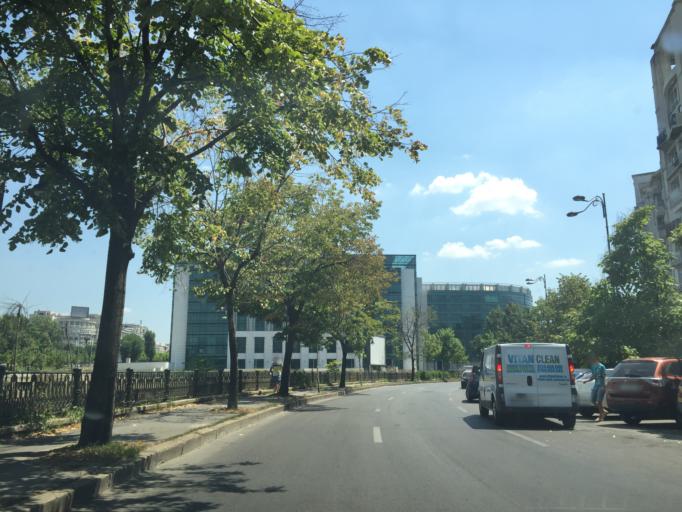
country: RO
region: Bucuresti
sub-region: Municipiul Bucuresti
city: Bucharest
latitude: 44.4256
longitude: 26.1069
